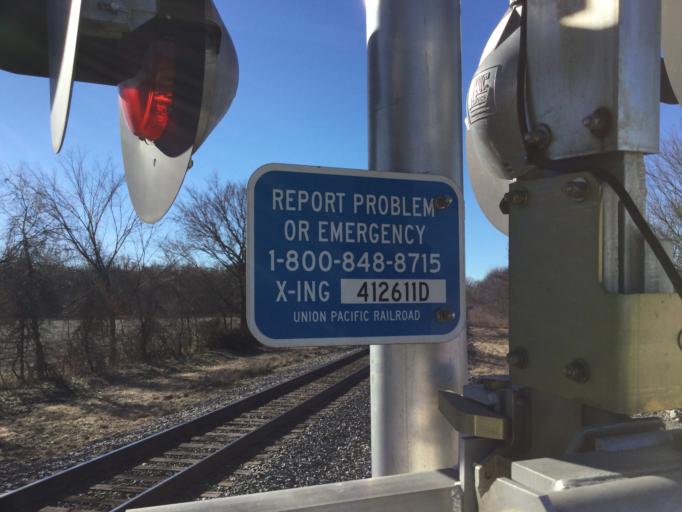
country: US
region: Kansas
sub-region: Miami County
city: Osawatomie
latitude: 38.3749
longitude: -94.9876
